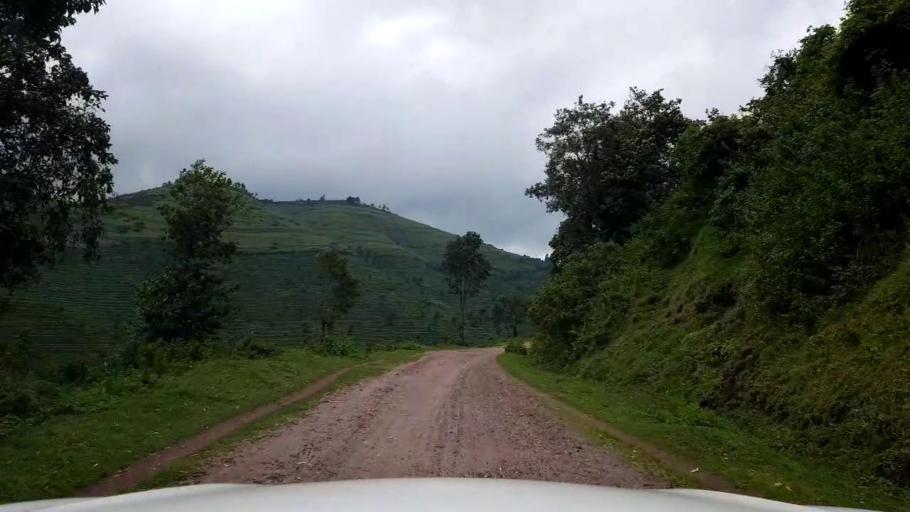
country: RW
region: Western Province
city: Gisenyi
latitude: -1.6653
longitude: 29.4178
